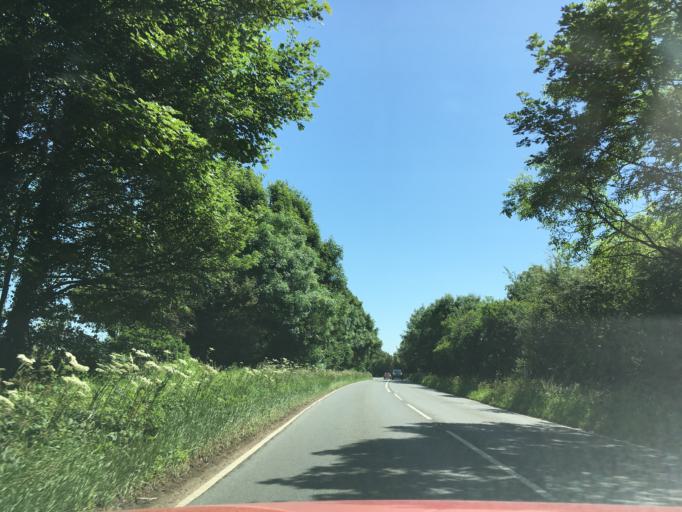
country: GB
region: England
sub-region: Oxfordshire
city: Hook Norton
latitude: 51.9700
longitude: -1.4703
